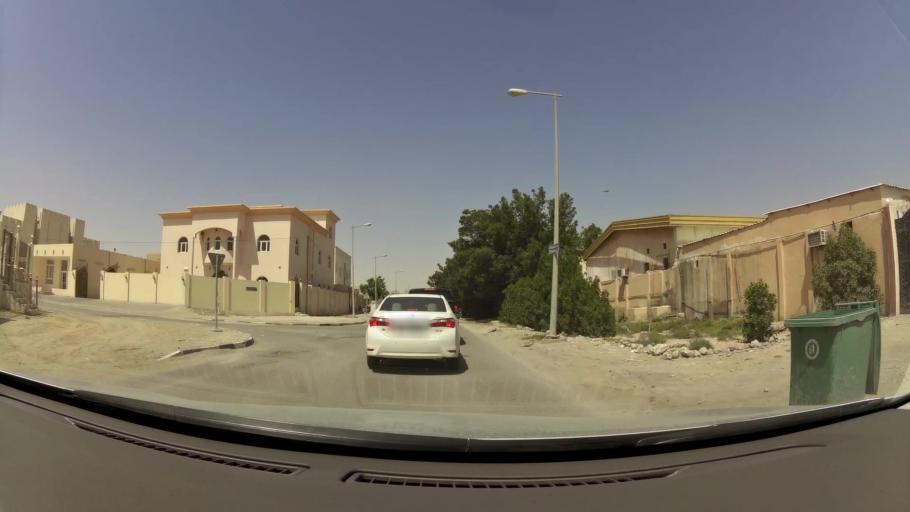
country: QA
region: Baladiyat ar Rayyan
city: Ar Rayyan
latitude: 25.2572
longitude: 51.4123
